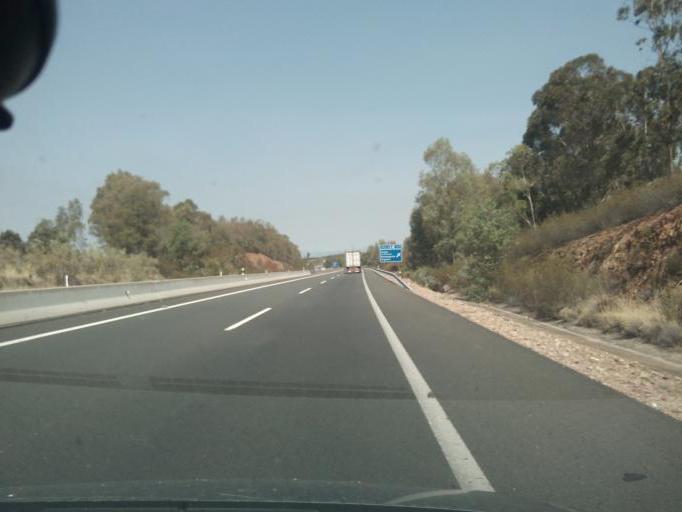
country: ES
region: Extremadura
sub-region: Provincia de Caceres
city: Romangordo
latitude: 39.7199
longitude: -5.7103
